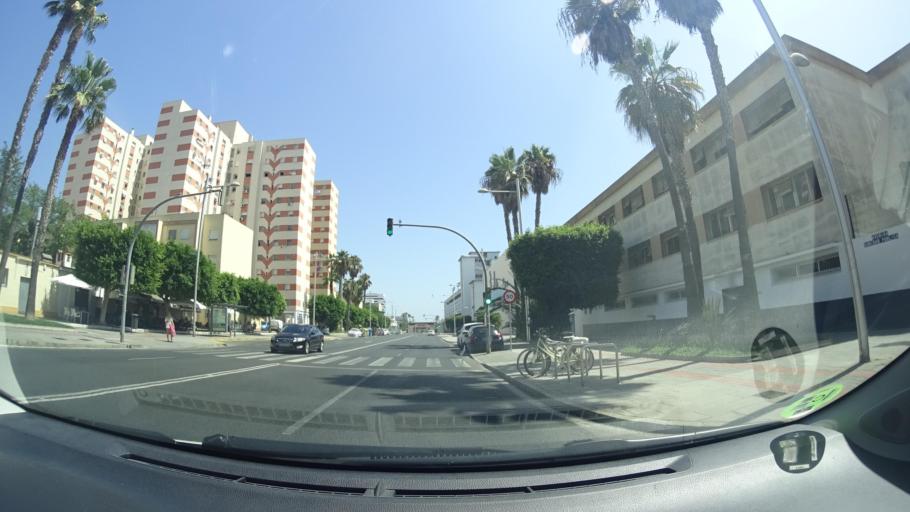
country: ES
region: Andalusia
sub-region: Provincia de Cadiz
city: Cadiz
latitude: 36.5053
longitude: -6.2732
